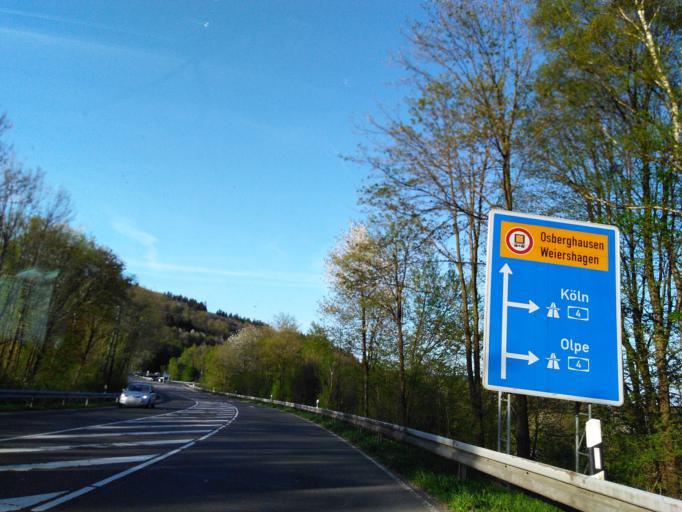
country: DE
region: North Rhine-Westphalia
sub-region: Regierungsbezirk Koln
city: Engelskirchen
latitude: 50.9717
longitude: 7.4621
